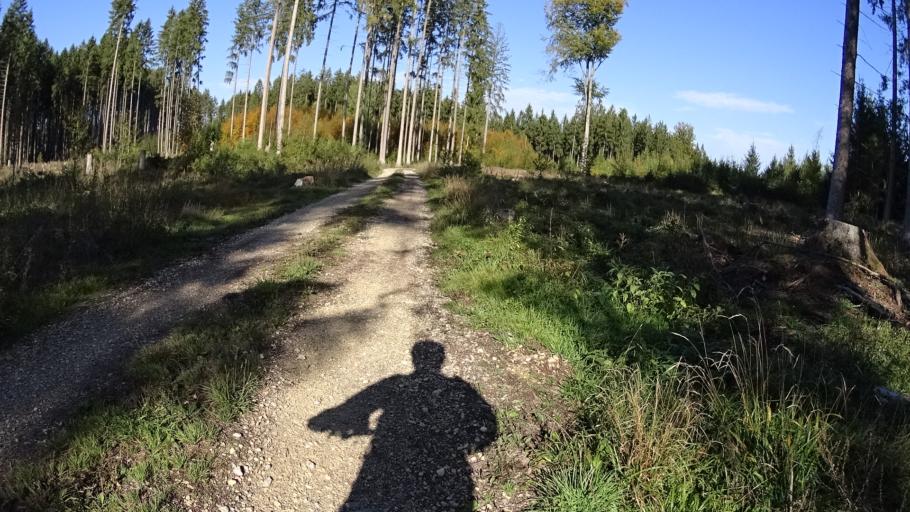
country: DE
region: Bavaria
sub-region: Upper Bavaria
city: Bohmfeld
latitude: 48.8831
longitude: 11.3637
